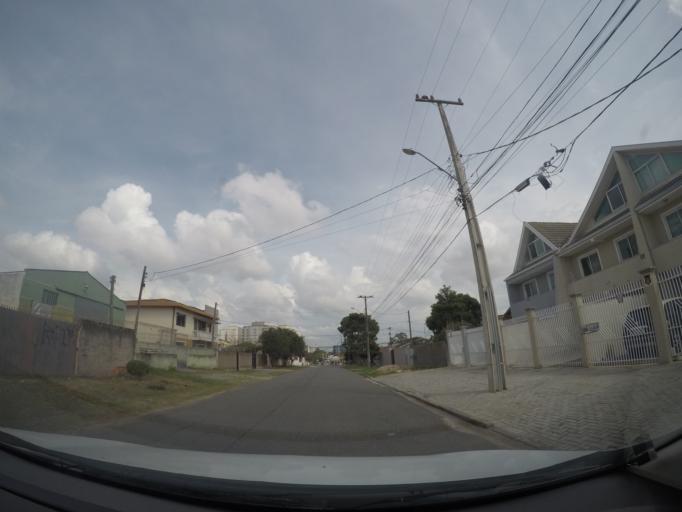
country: BR
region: Parana
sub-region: Curitiba
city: Curitiba
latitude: -25.4889
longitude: -49.2719
